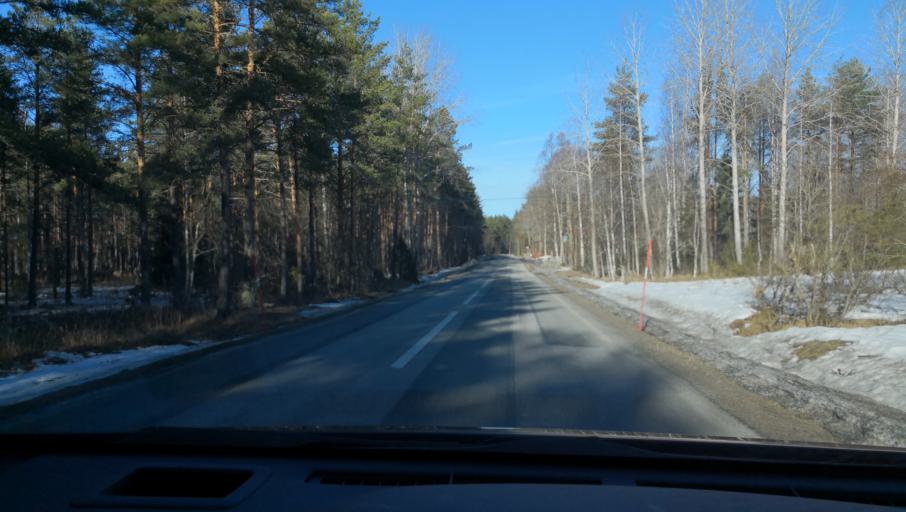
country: SE
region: Uppsala
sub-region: Osthammars Kommun
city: Osterbybruk
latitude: 60.2658
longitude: 17.9552
